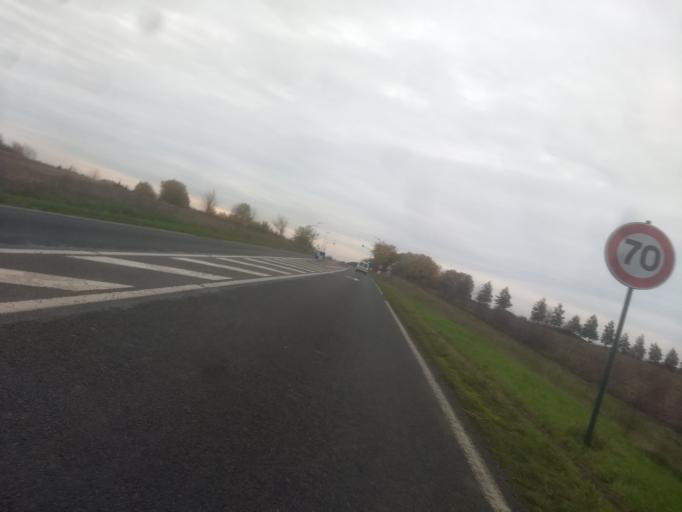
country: FR
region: Nord-Pas-de-Calais
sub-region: Departement du Pas-de-Calais
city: Achicourt
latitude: 50.2734
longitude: 2.7445
